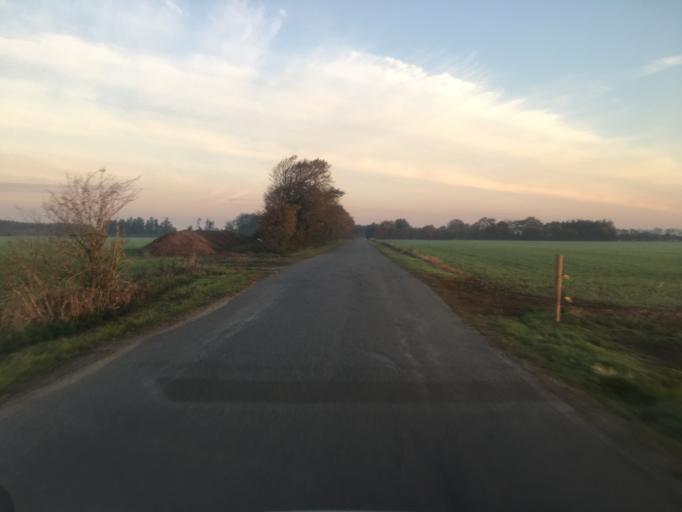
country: DK
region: South Denmark
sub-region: Tonder Kommune
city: Logumkloster
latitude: 55.0170
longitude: 9.0467
